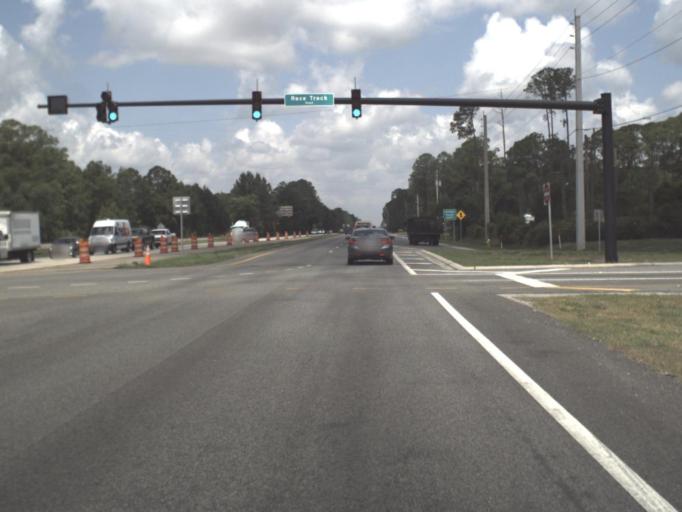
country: US
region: Florida
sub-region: Saint Johns County
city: Palm Valley
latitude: 30.1047
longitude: -81.4788
